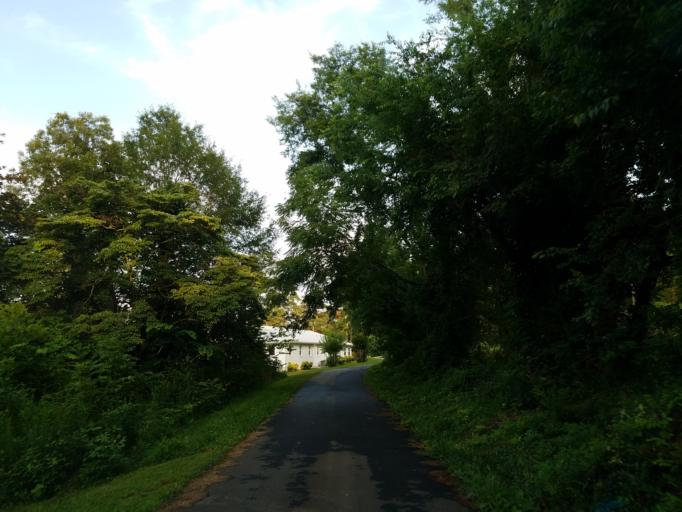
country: US
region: Georgia
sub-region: Pickens County
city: Nelson
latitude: 34.4165
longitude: -84.3875
